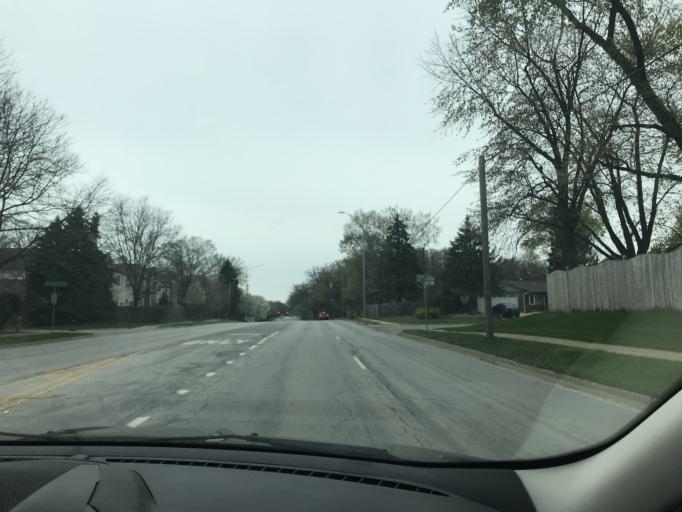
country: US
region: Illinois
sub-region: DuPage County
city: Naperville
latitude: 41.7383
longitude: -88.1177
